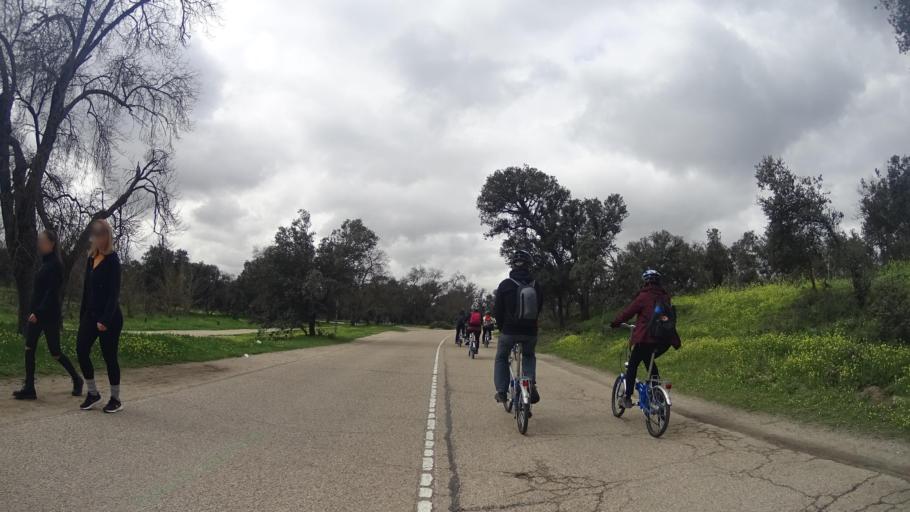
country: ES
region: Madrid
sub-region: Provincia de Madrid
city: Latina
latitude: 40.4143
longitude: -3.7555
